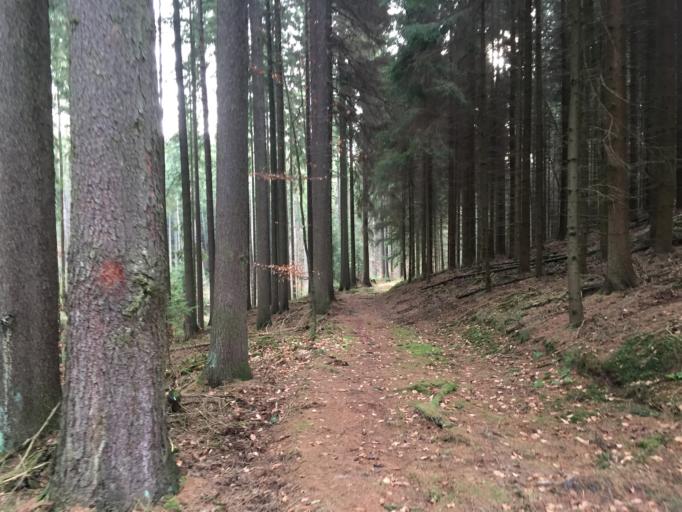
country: DE
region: Thuringia
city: Bollberg
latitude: 50.8914
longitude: 11.7928
